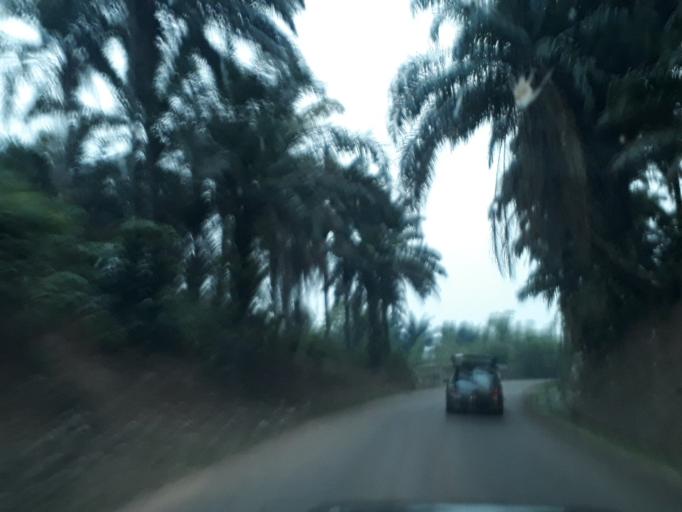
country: CD
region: Bandundu
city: Kikwit
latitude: -5.0803
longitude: 18.8839
